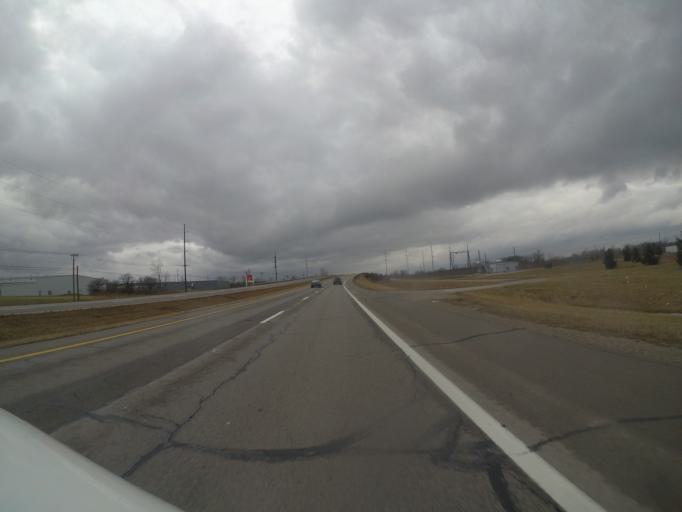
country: US
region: Ohio
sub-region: Wood County
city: Rossford
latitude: 41.5639
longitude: -83.5463
